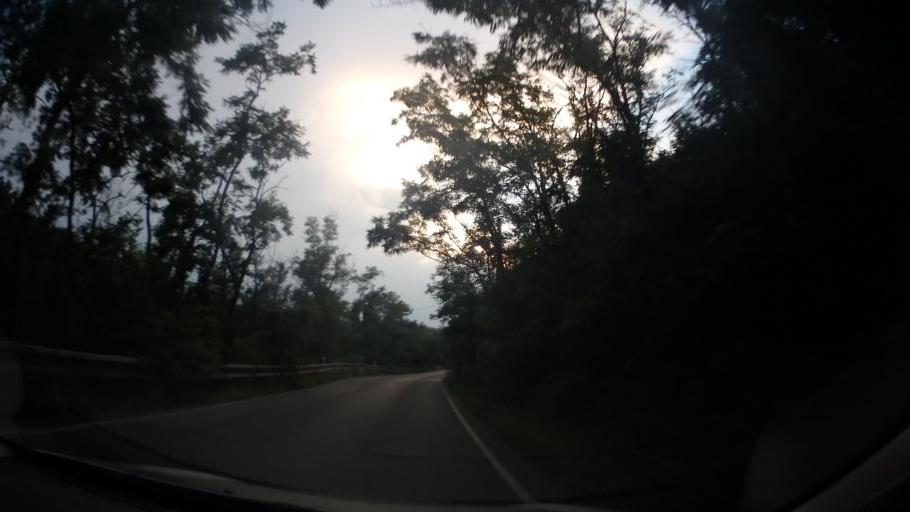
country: CZ
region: South Moravian
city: Dolni Kounice
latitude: 49.0712
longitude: 16.4755
